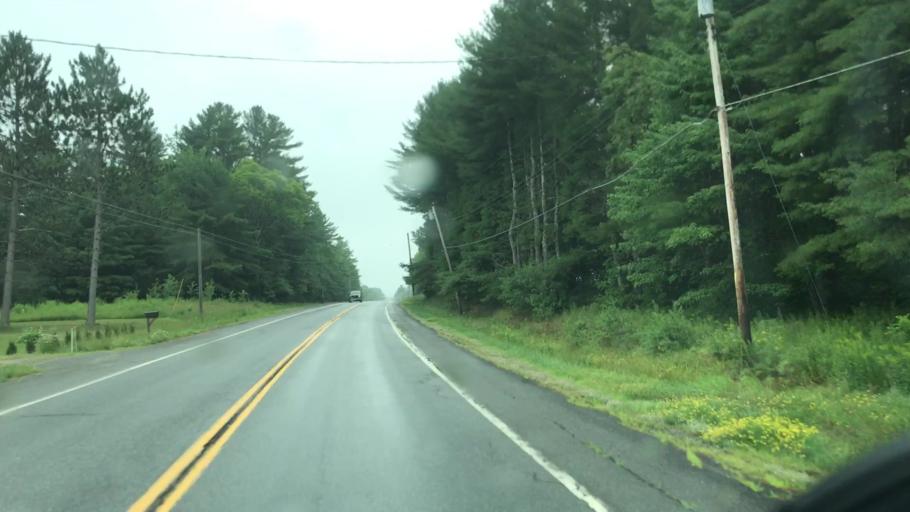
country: US
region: Maine
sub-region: Penobscot County
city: Howland
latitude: 45.2867
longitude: -68.6250
